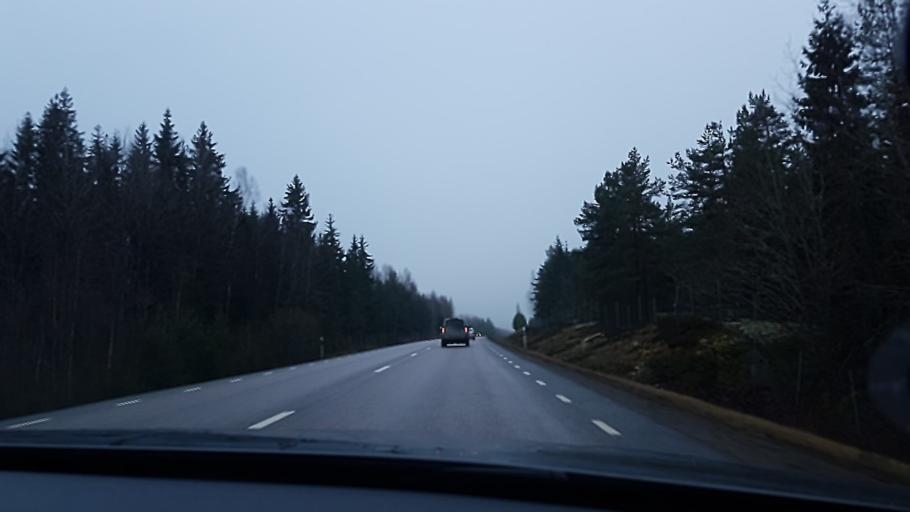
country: SE
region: Vaestra Goetaland
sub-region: Toreboda Kommun
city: Toereboda
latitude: 58.8250
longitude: 13.9879
